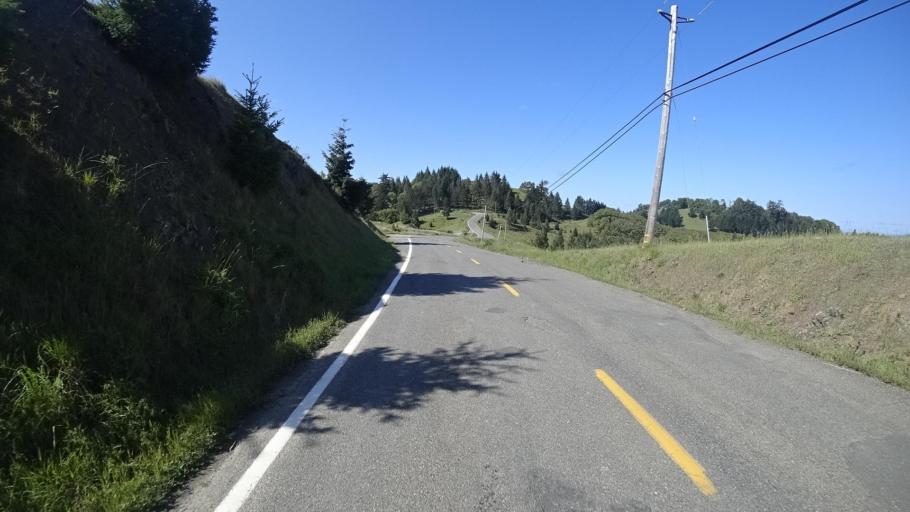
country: US
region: California
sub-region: Humboldt County
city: Redway
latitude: 40.1100
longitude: -123.7450
